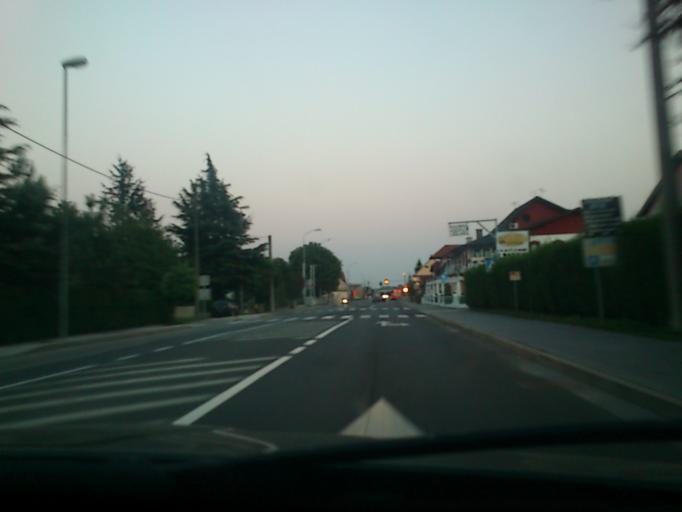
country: SI
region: Miklavz na Dravskem Polju
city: Miklavz na Dravskem Polju
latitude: 46.5035
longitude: 15.7011
